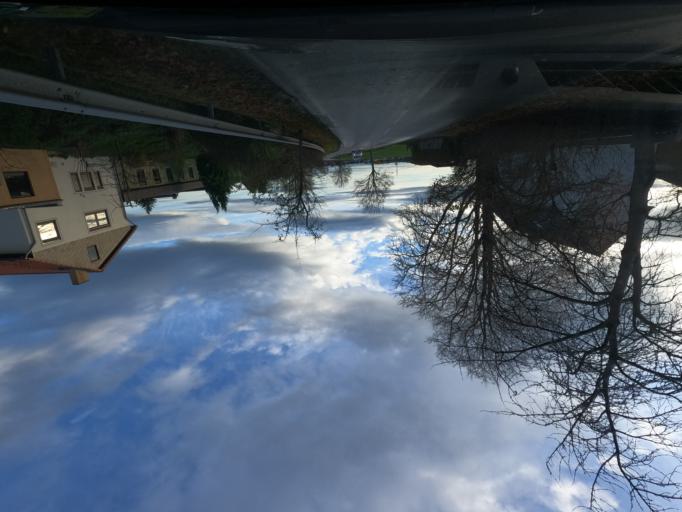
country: DE
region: Lower Saxony
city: Kissenbruck
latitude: 52.1511
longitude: 10.5915
